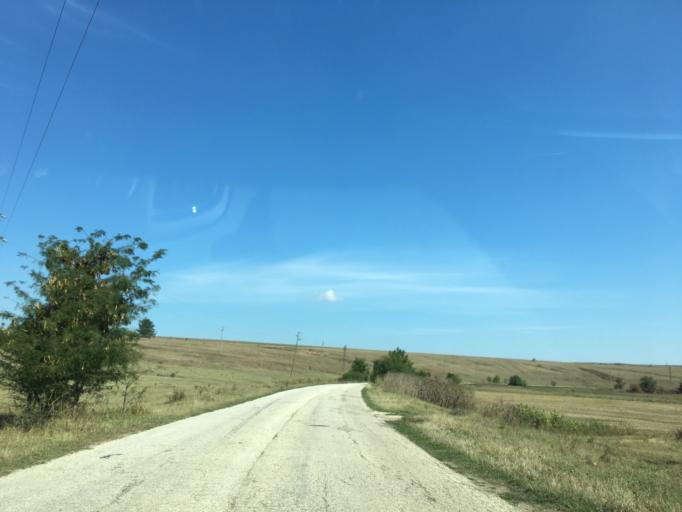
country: BG
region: Pleven
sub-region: Obshtina Knezha
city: Knezha
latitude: 43.5377
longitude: 24.1032
